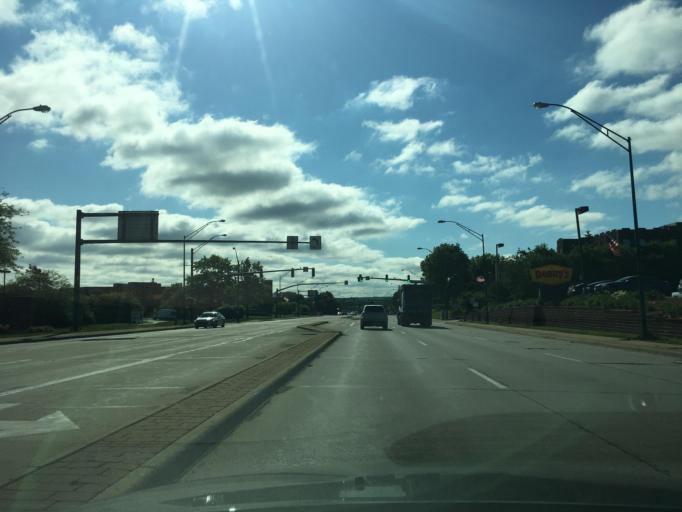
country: US
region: Ohio
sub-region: Cuyahoga County
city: Seven Hills
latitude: 41.3958
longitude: -81.6489
